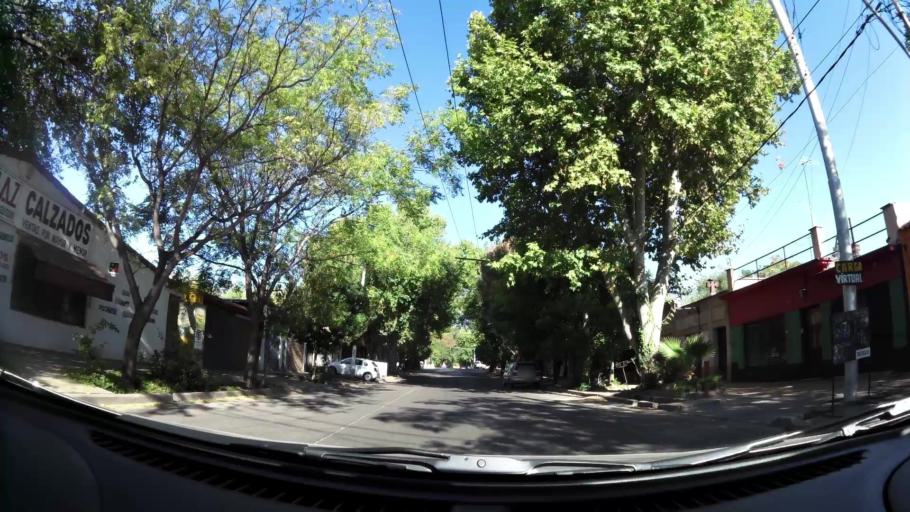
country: AR
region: Mendoza
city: Las Heras
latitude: -32.8659
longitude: -68.8427
